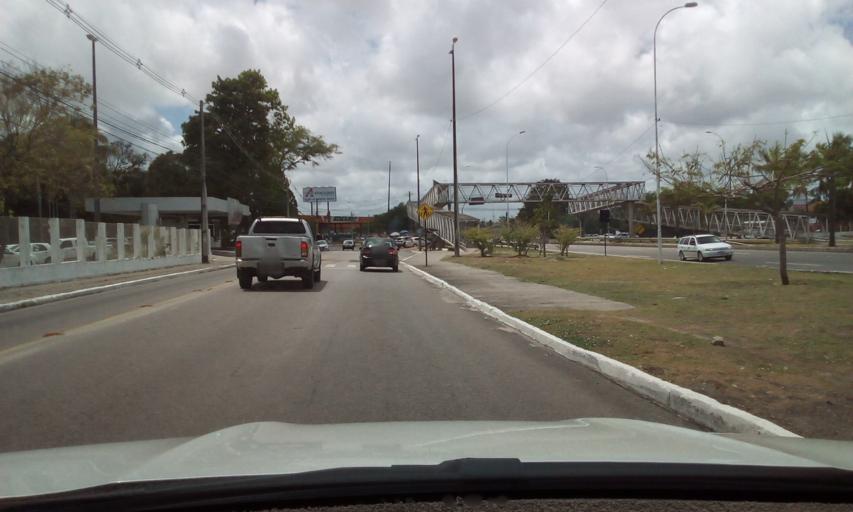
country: BR
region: Paraiba
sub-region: Joao Pessoa
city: Joao Pessoa
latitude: -7.1678
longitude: -34.8639
